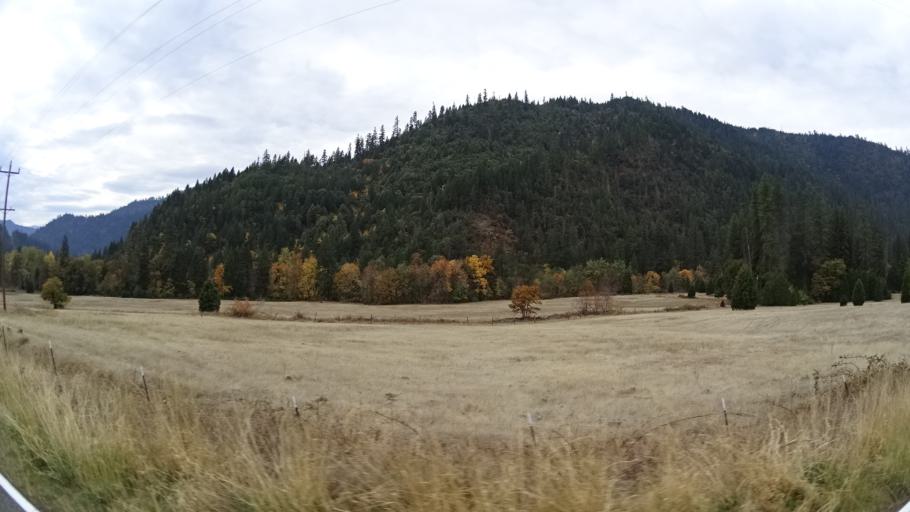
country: US
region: California
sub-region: Siskiyou County
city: Happy Camp
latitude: 41.8741
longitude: -123.4112
